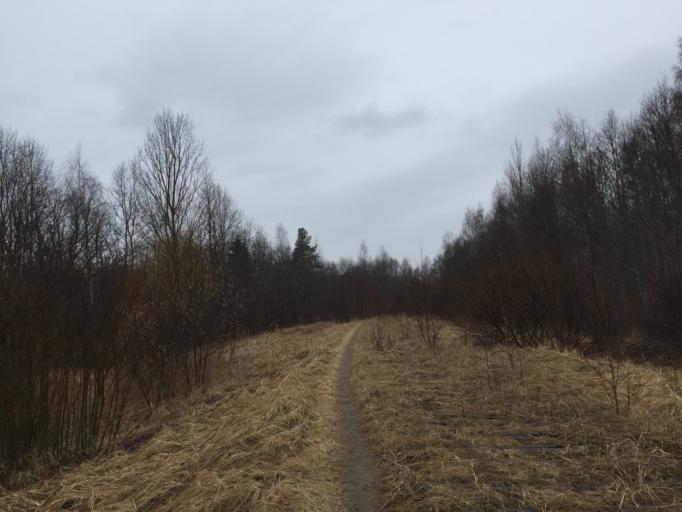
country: LV
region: Lielvarde
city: Lielvarde
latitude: 56.7263
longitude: 24.7803
